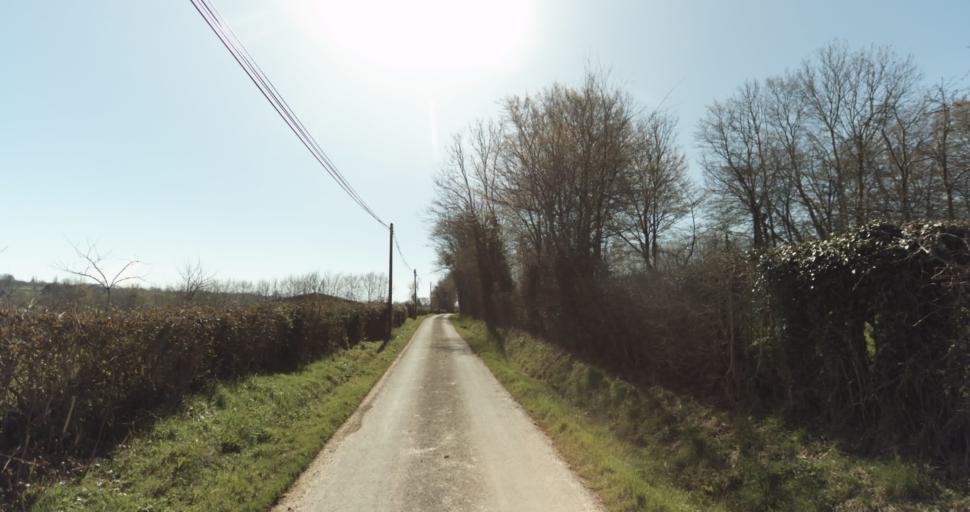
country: FR
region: Lower Normandy
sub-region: Departement du Calvados
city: Livarot
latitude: 49.0049
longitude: 0.0881
